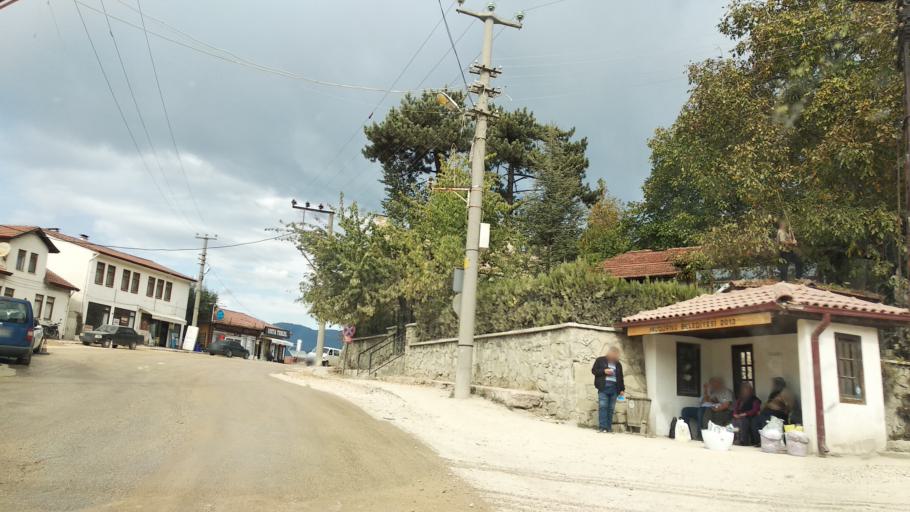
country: TR
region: Bolu
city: Mudurnu
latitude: 40.4689
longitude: 31.2101
